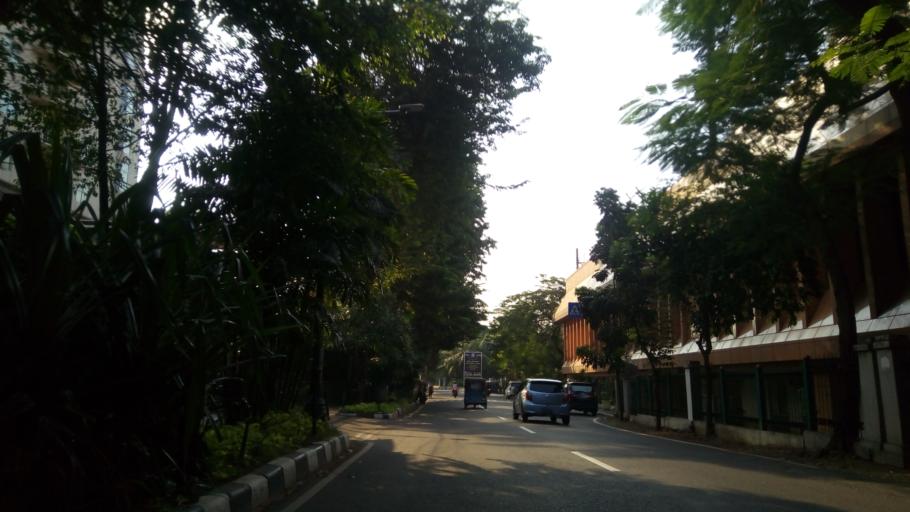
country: ID
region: Jakarta Raya
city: Jakarta
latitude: -6.1982
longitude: 106.8410
